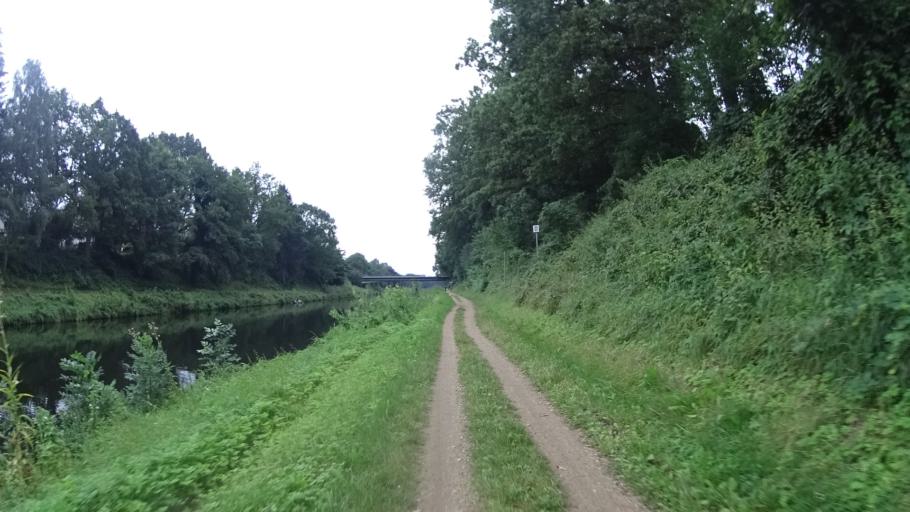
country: DE
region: Schleswig-Holstein
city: Molln
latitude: 53.6236
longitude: 10.6741
